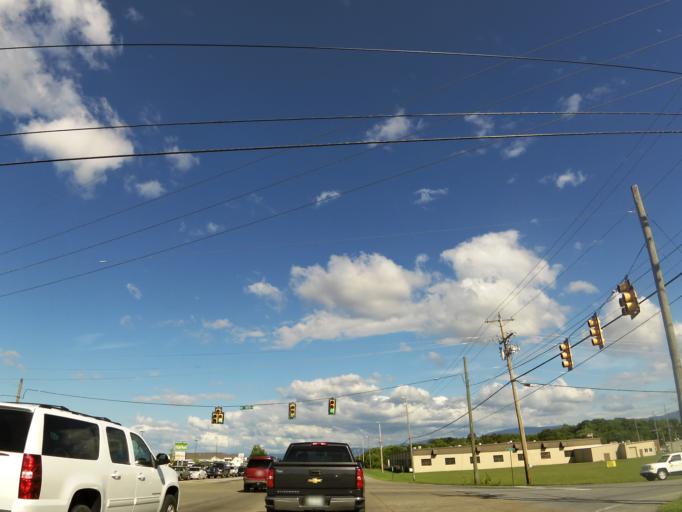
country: US
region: Tennessee
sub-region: Greene County
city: Greeneville
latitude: 36.1791
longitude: -82.8100
